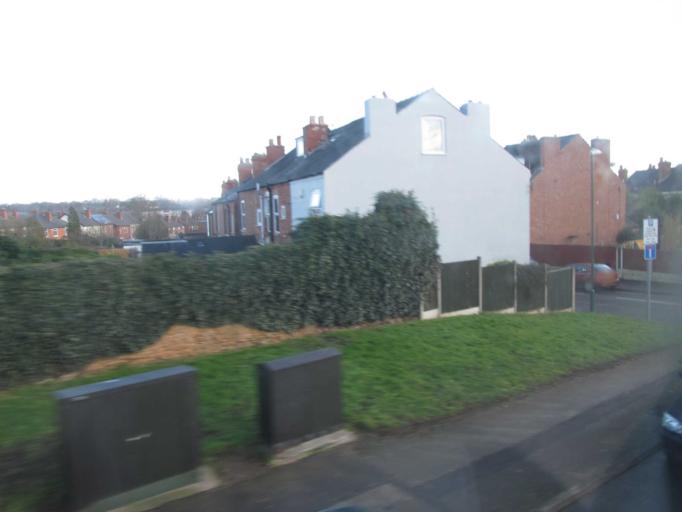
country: GB
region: England
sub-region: Nottinghamshire
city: Hucknall
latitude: 53.0059
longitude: -1.1988
